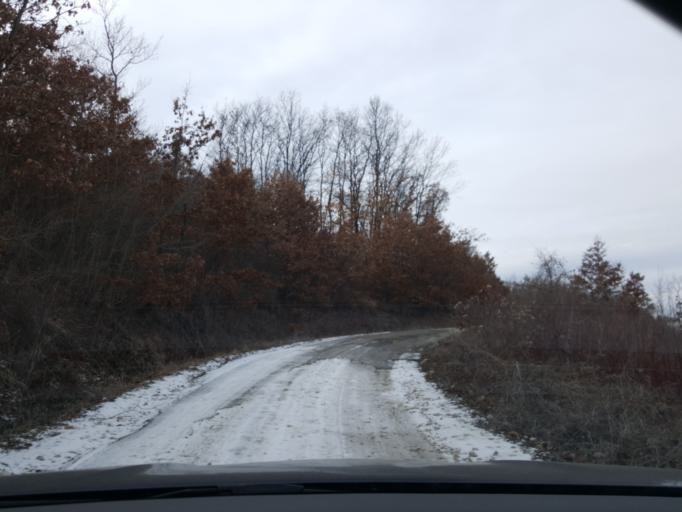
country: RS
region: Central Serbia
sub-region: Pirotski Okrug
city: Dimitrovgrad
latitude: 43.0044
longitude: 22.7483
